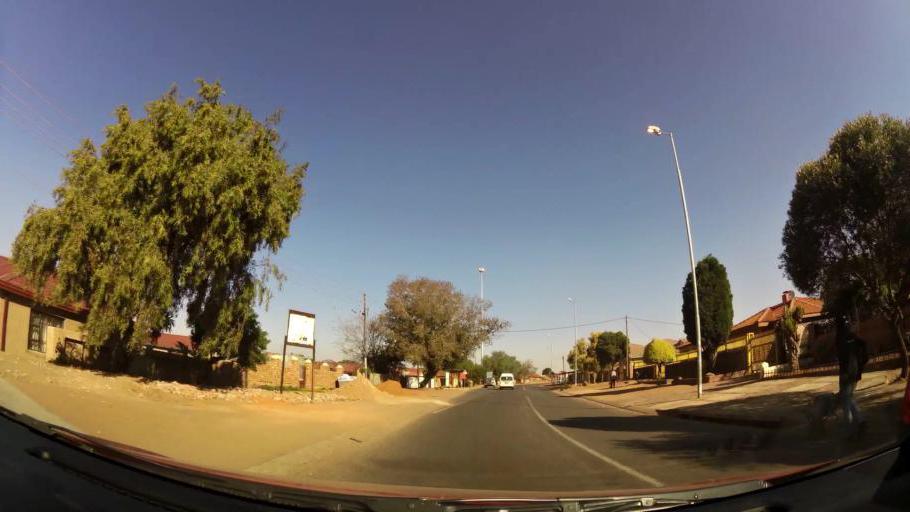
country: ZA
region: Gauteng
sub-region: City of Tshwane Metropolitan Municipality
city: Mabopane
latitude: -25.5368
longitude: 28.1062
